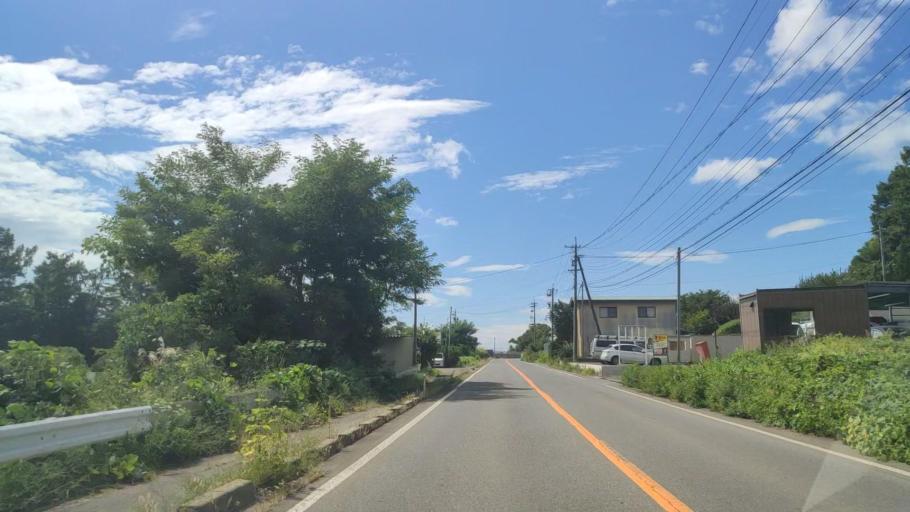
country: JP
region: Nagano
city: Nakano
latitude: 36.7477
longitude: 138.3137
